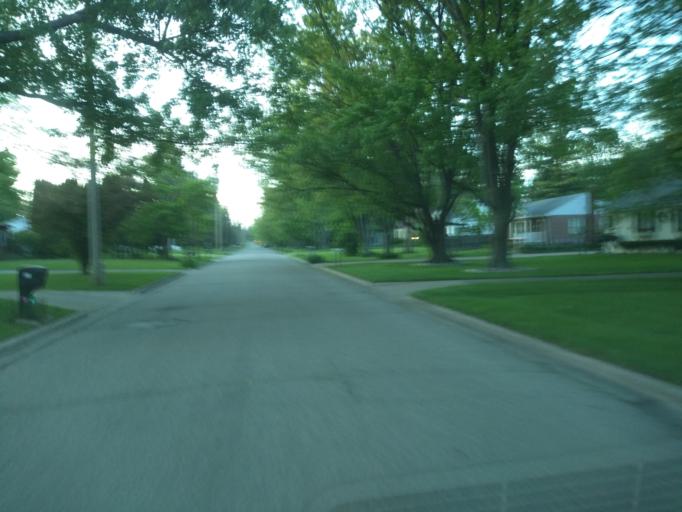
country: US
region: Michigan
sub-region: Eaton County
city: Waverly
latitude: 42.7441
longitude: -84.6090
